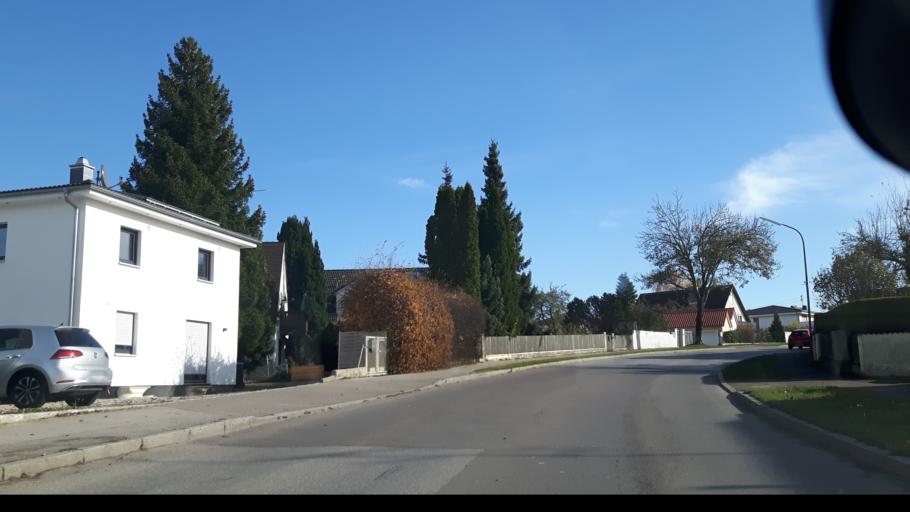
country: DE
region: Bavaria
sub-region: Upper Bavaria
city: Schwabhausen
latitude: 48.3029
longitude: 11.3600
